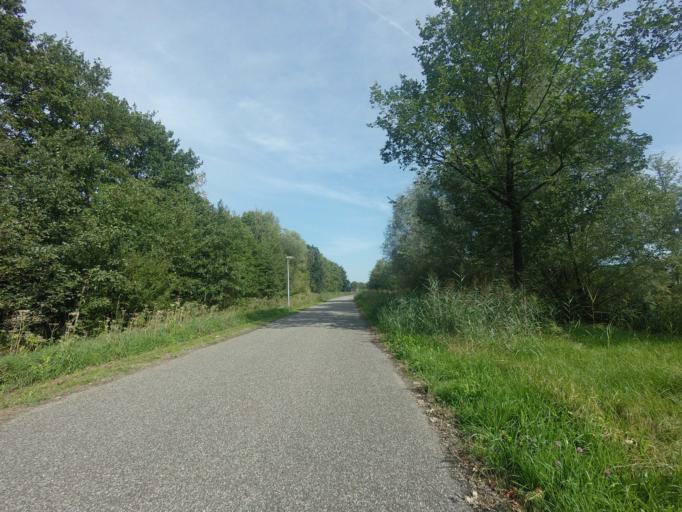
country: NL
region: Groningen
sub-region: Gemeente Leek
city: Leek
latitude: 53.1802
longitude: 6.3801
